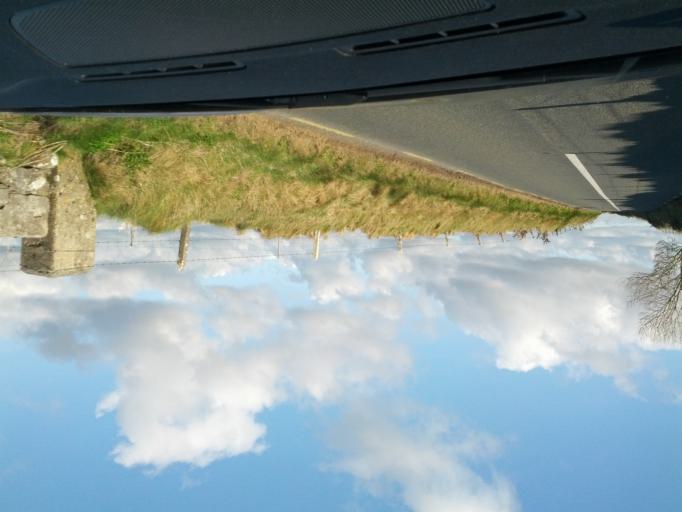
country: IE
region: Connaught
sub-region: Roscommon
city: Castlerea
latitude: 53.5634
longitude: -8.5713
